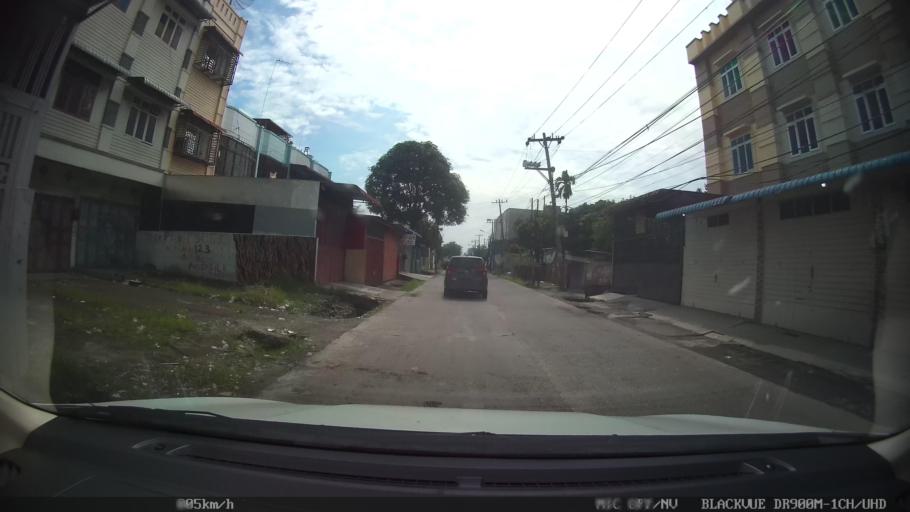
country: ID
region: North Sumatra
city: Medan
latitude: 3.5875
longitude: 98.7116
